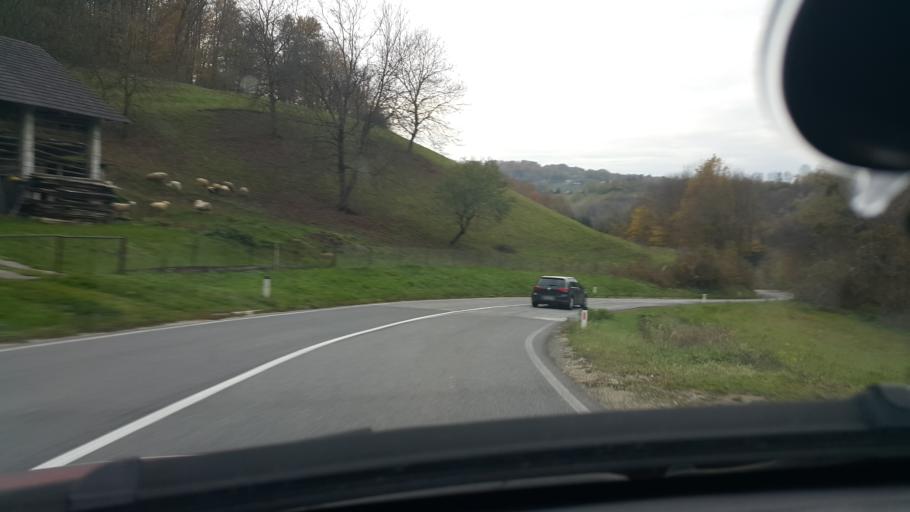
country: SI
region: Bistrica ob Sotli
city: Bistrica ob Sotli
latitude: 46.0765
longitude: 15.6343
